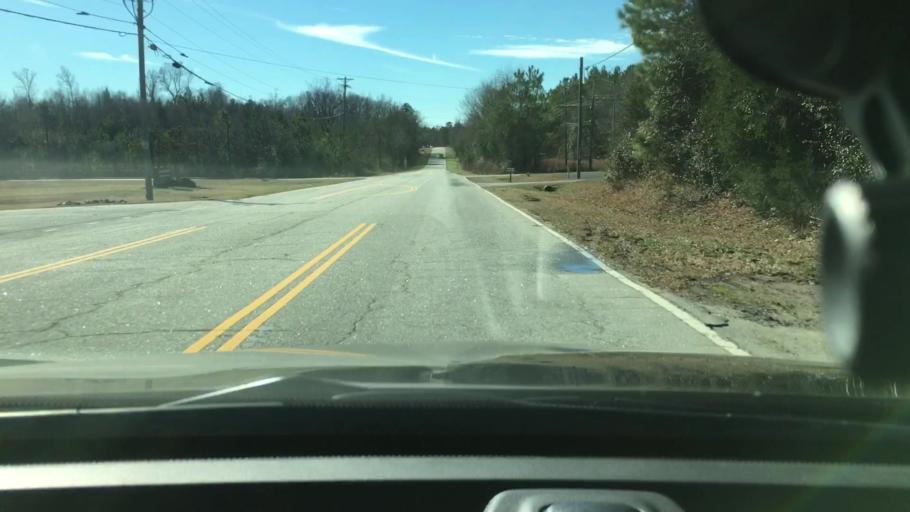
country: US
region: South Carolina
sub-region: Cherokee County
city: Gaffney
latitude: 35.0499
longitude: -81.6720
